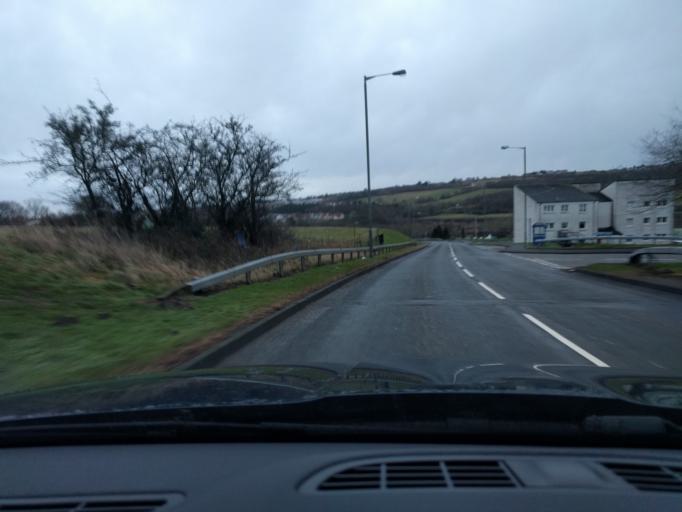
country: GB
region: Scotland
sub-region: Falkirk
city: Falkirk
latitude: 55.9876
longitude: -3.7667
